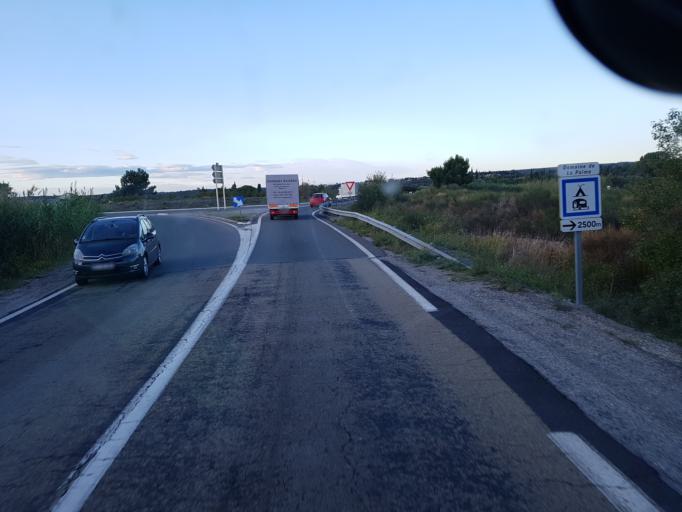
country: FR
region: Languedoc-Roussillon
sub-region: Departement de l'Aude
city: Leucate
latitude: 42.9580
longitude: 2.9853
